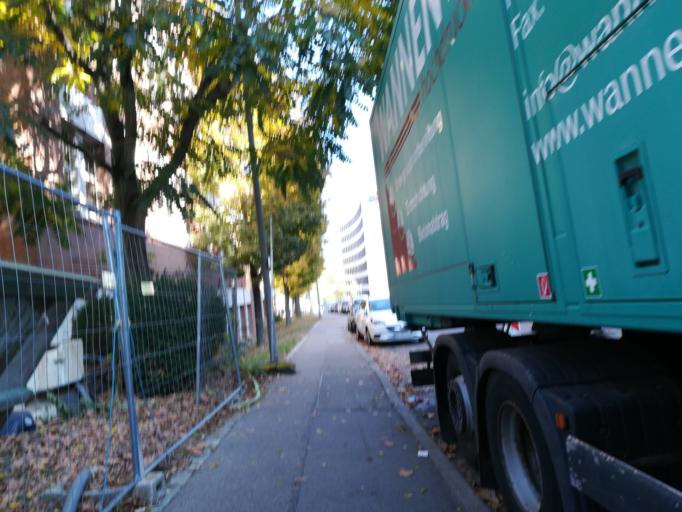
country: DE
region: Baden-Wuerttemberg
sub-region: Regierungsbezirk Stuttgart
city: Stuttgart Feuerbach
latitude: 48.8122
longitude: 9.1779
